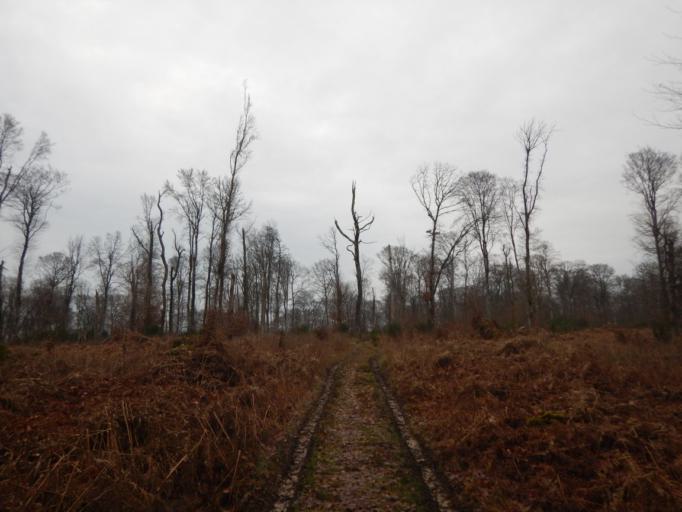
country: LU
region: Luxembourg
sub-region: Canton de Capellen
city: Koerich
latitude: 49.6846
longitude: 5.9591
